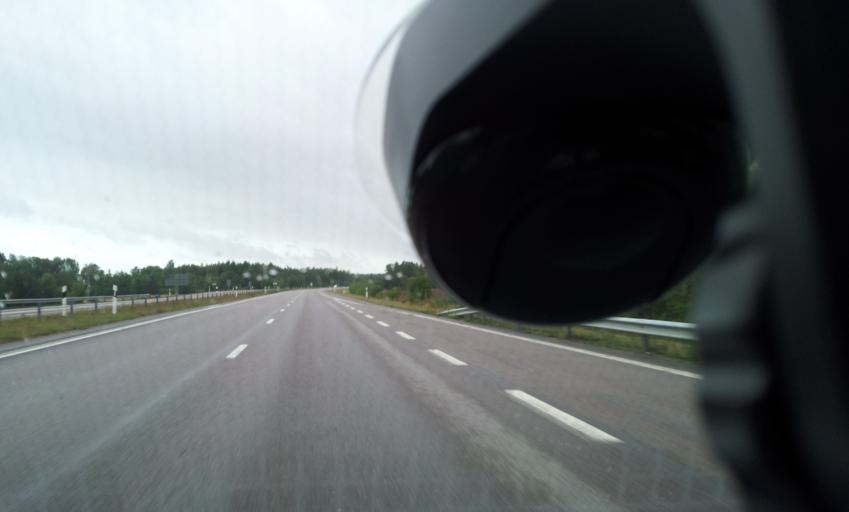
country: SE
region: Kalmar
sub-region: Kalmar Kommun
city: Ljungbyholm
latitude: 56.6365
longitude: 16.2121
